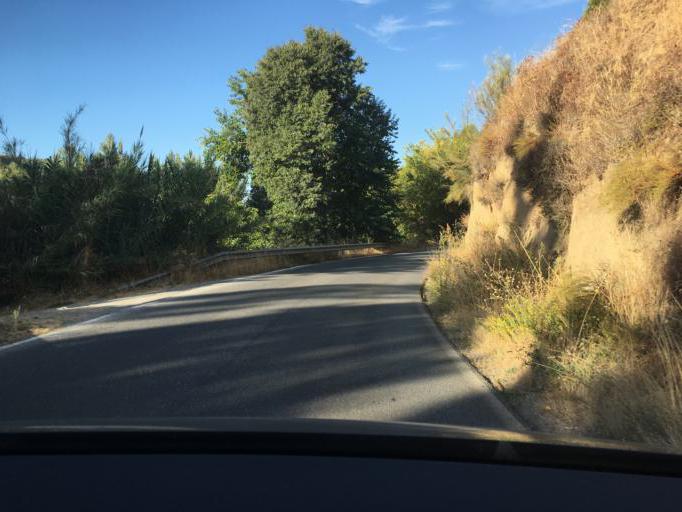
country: ES
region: Andalusia
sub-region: Provincia de Granada
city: Dudar
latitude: 37.1890
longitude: -3.4760
